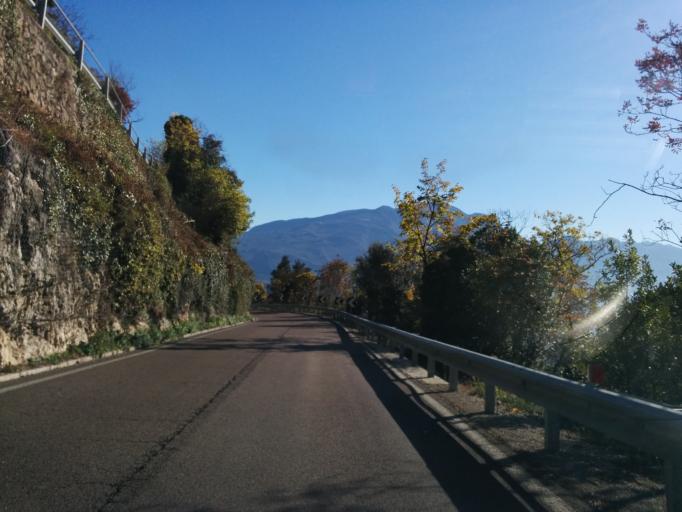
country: IT
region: Trentino-Alto Adige
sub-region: Provincia di Trento
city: Tenno
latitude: 45.9168
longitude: 10.8350
